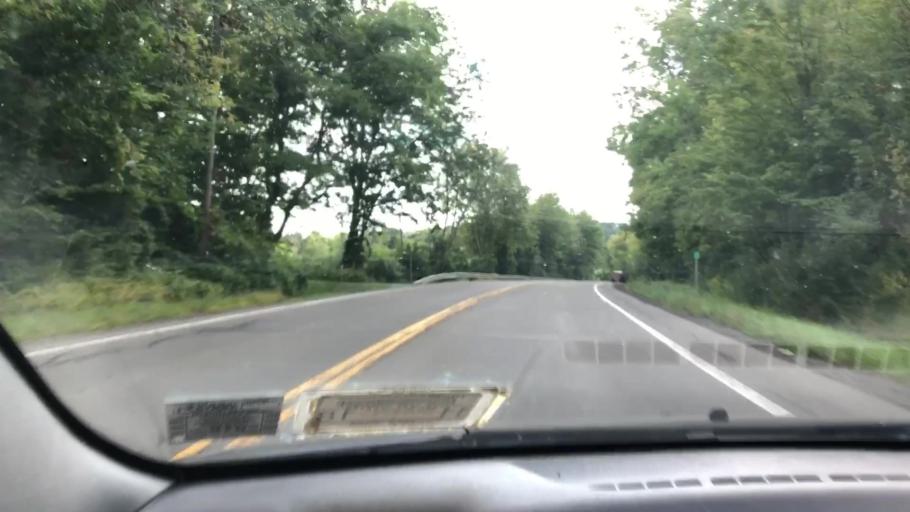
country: US
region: New York
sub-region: Wayne County
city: Macedon
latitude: 43.0955
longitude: -77.3613
